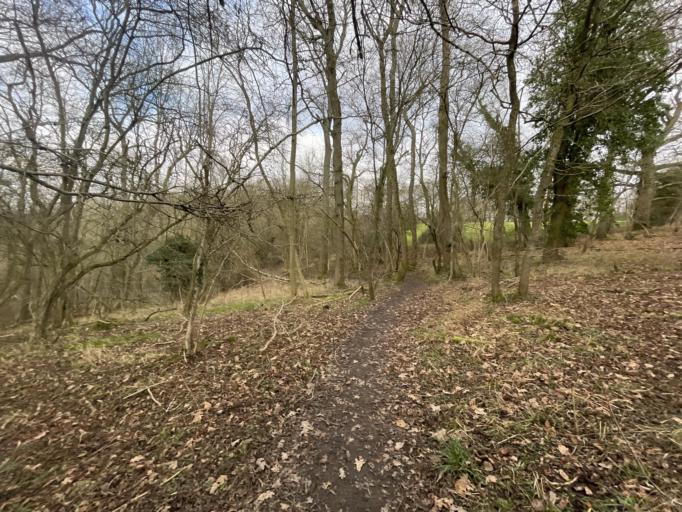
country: GB
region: England
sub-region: West Berkshire
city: Calcot
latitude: 51.4535
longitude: -1.0629
